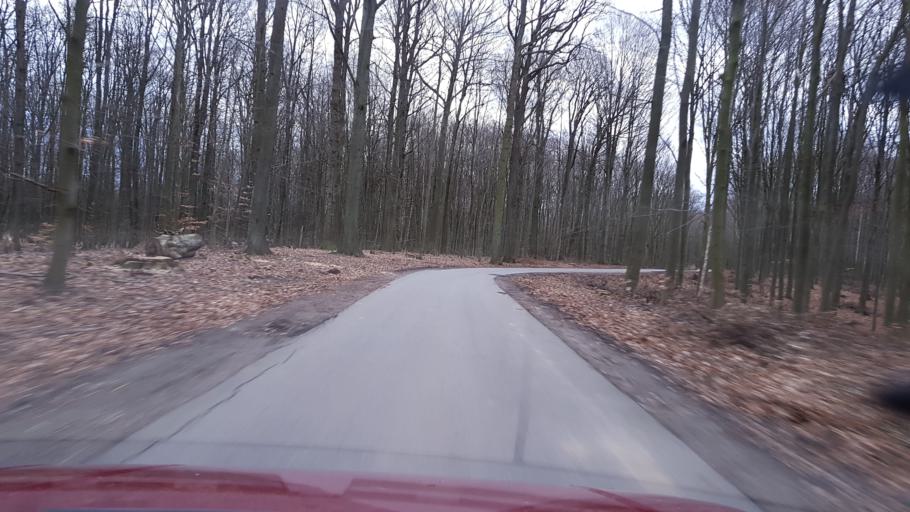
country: PL
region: West Pomeranian Voivodeship
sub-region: Powiat gryfinski
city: Stare Czarnowo
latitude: 53.3144
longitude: 14.7164
